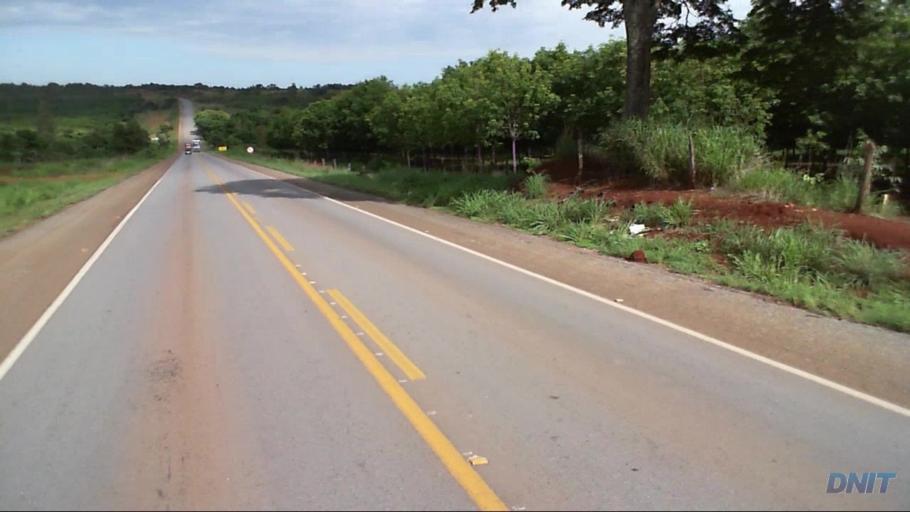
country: BR
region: Goias
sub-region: Barro Alto
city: Barro Alto
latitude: -14.8736
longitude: -49.0008
